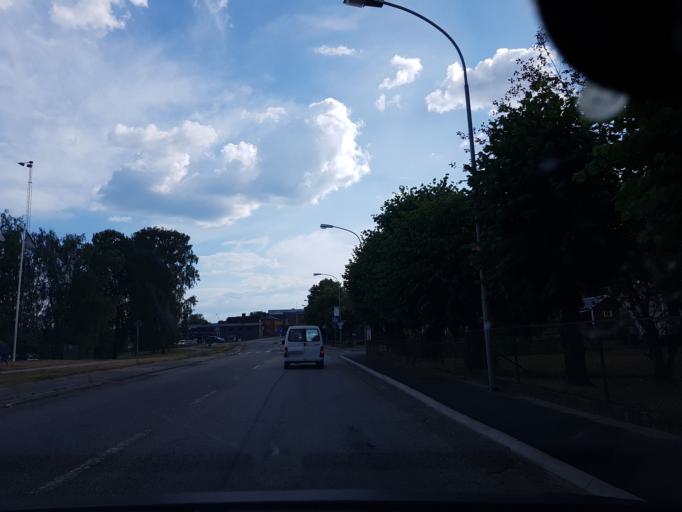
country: SE
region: Joenkoeping
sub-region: Gislaveds Kommun
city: Gislaved
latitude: 57.3070
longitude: 13.5416
